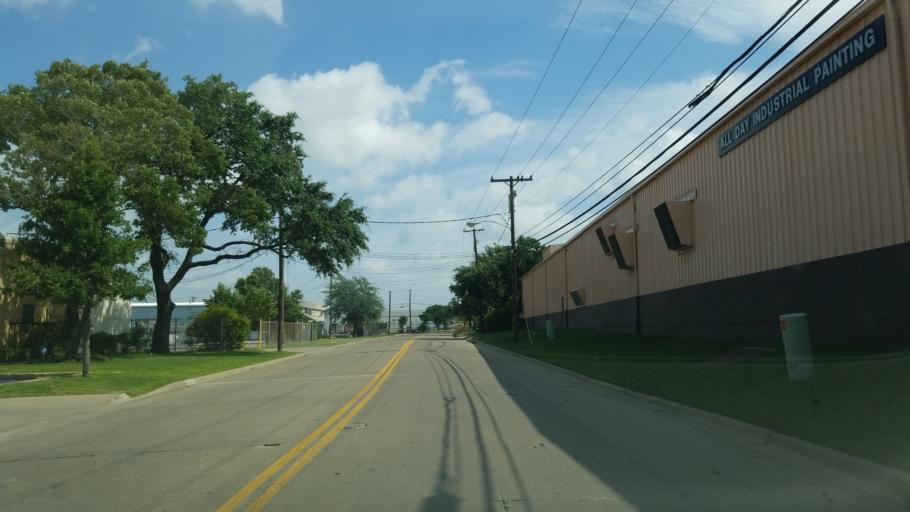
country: US
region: Texas
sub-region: Dallas County
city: Farmers Branch
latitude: 32.8722
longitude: -96.8905
